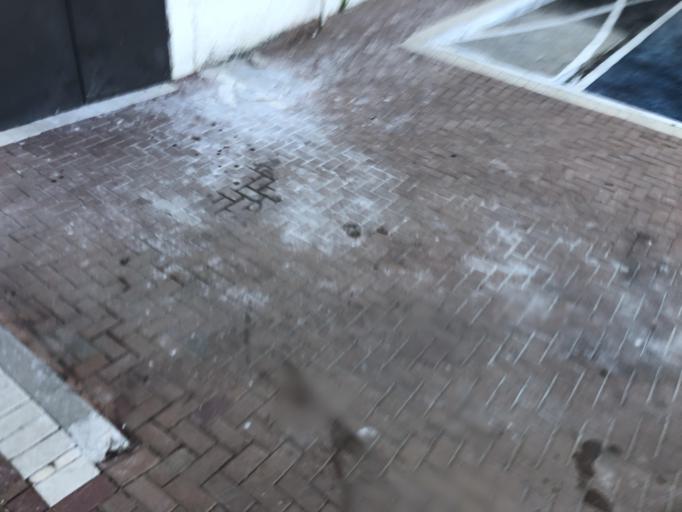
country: IL
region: Central District
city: Yehud
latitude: 32.0406
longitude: 34.8923
